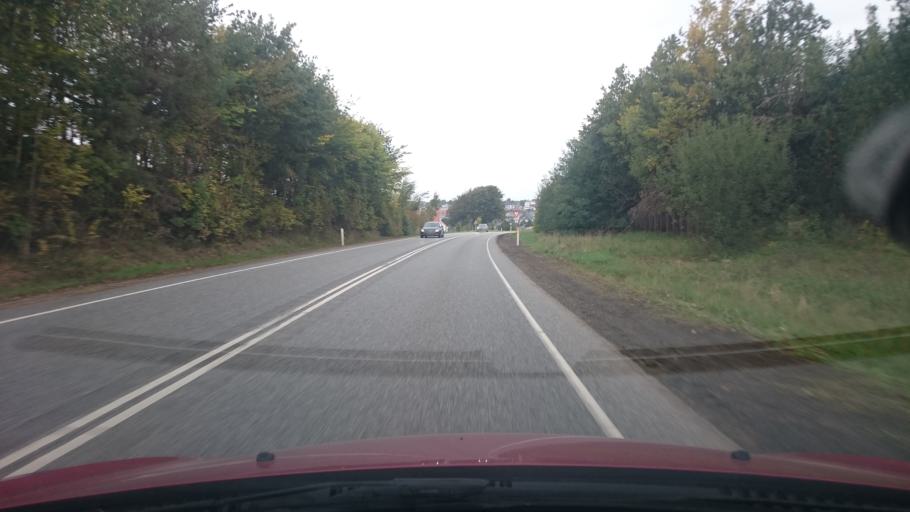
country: DK
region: North Denmark
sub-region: Mariagerfjord Kommune
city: Hadsund
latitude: 56.7064
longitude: 10.1229
